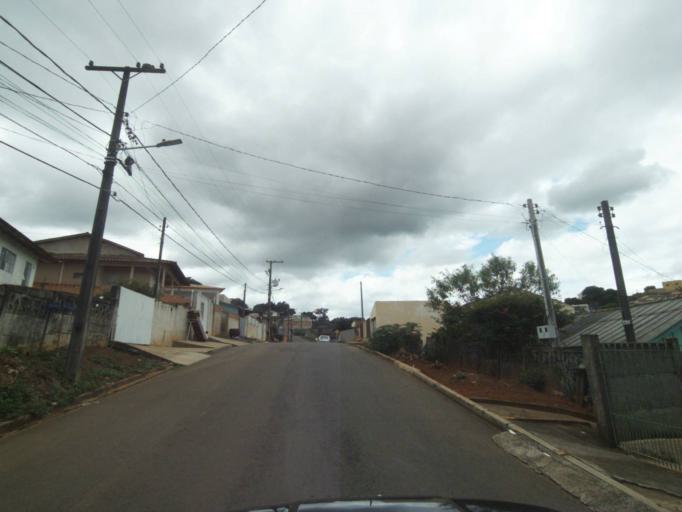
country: BR
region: Parana
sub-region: Telemaco Borba
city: Telemaco Borba
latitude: -24.3254
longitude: -50.6358
